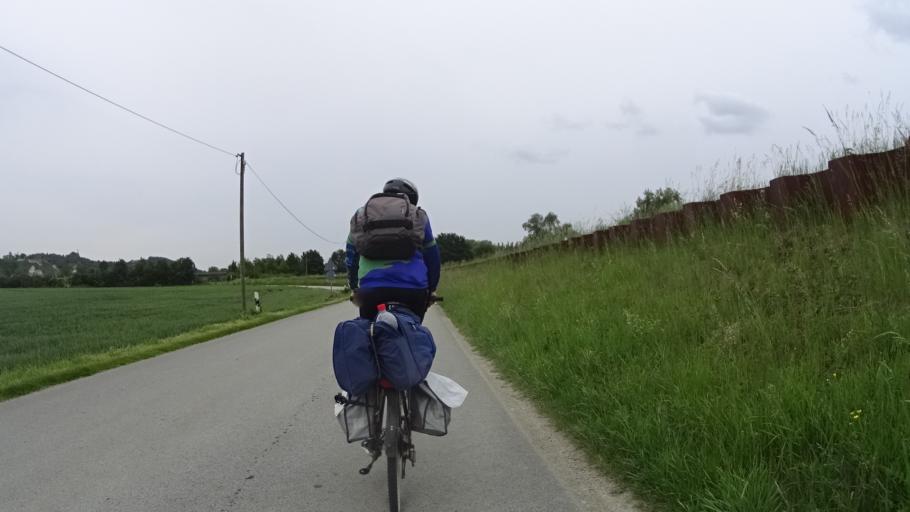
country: DE
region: Bavaria
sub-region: Lower Bavaria
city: Winzer
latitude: 48.7288
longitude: 13.0576
